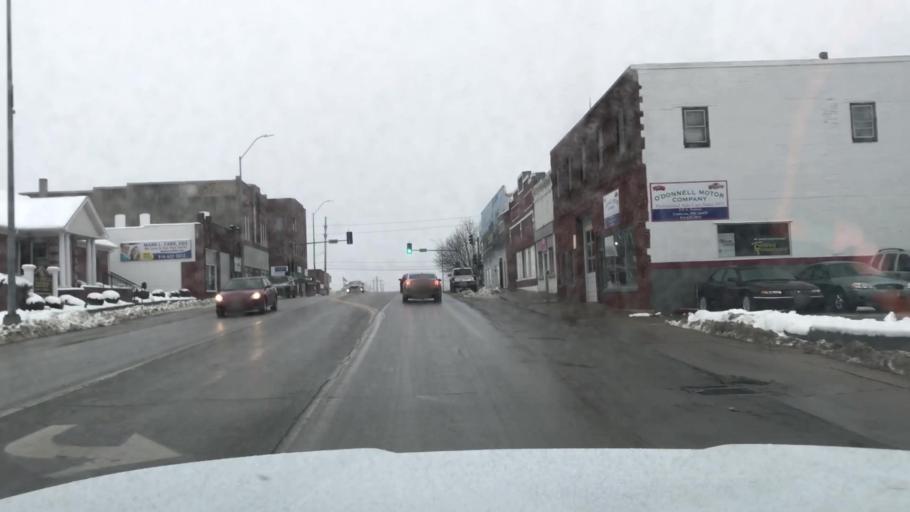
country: US
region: Missouri
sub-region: Clinton County
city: Cameron
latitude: 39.7421
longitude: -94.2359
